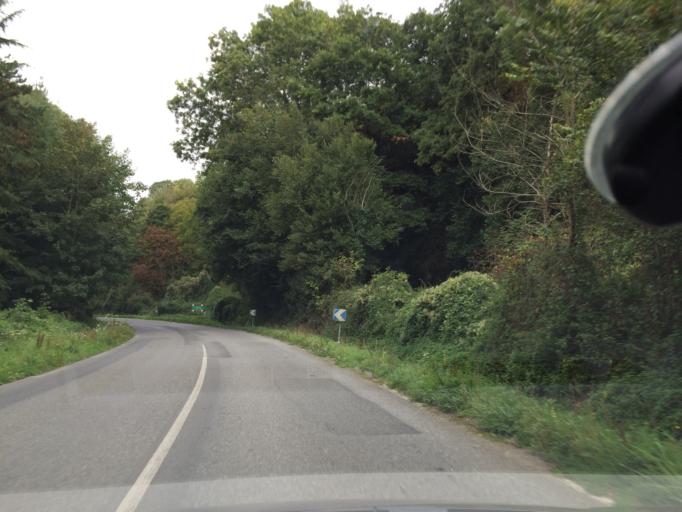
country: FR
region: Brittany
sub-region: Departement d'Ille-et-Vilaine
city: Hede-Bazouges
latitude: 48.2945
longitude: -1.8042
